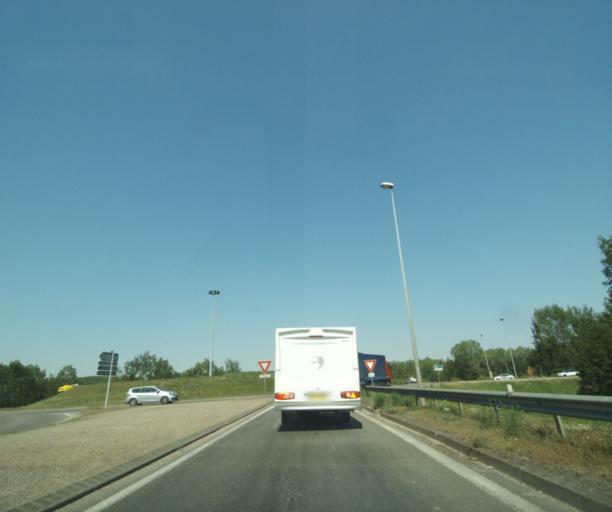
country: FR
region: Champagne-Ardenne
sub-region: Departement de la Marne
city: Vitry-le-Francois
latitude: 48.7404
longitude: 4.5930
